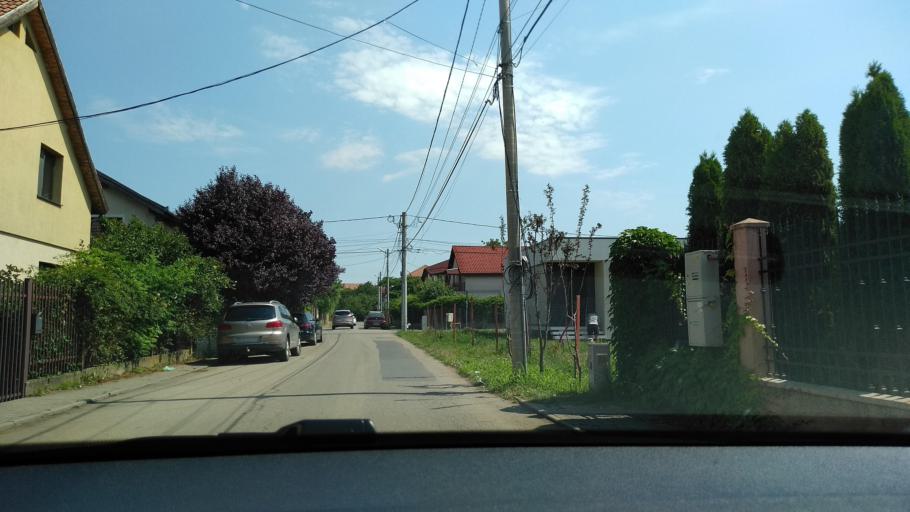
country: RO
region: Timis
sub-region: Comuna Dumbravita
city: Dumbravita
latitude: 45.7910
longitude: 21.2310
